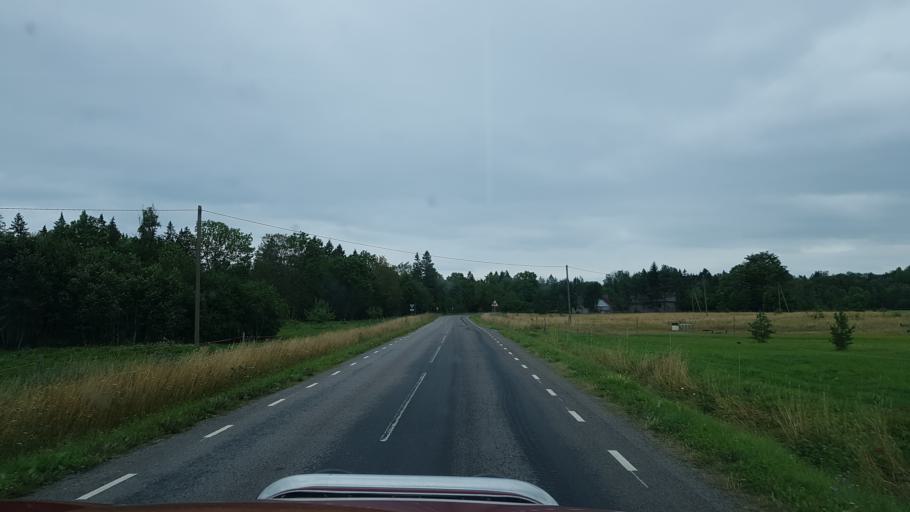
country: EE
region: Ida-Virumaa
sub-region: Johvi vald
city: Johvi
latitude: 59.4375
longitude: 27.4001
